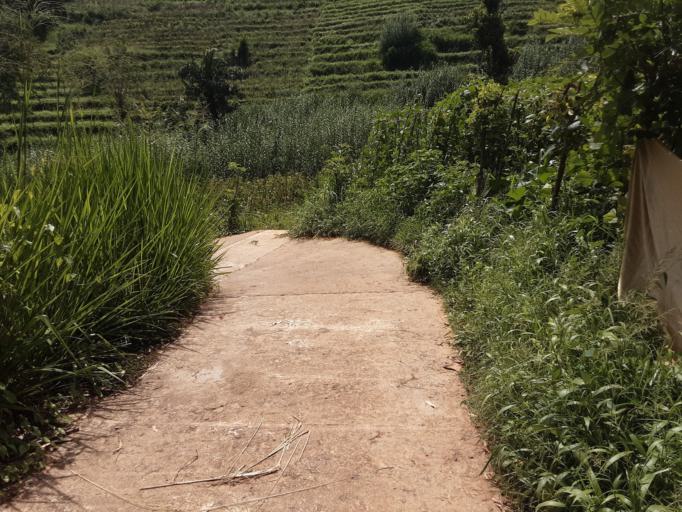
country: LK
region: Uva
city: Haputale
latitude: 6.8927
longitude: 80.9258
